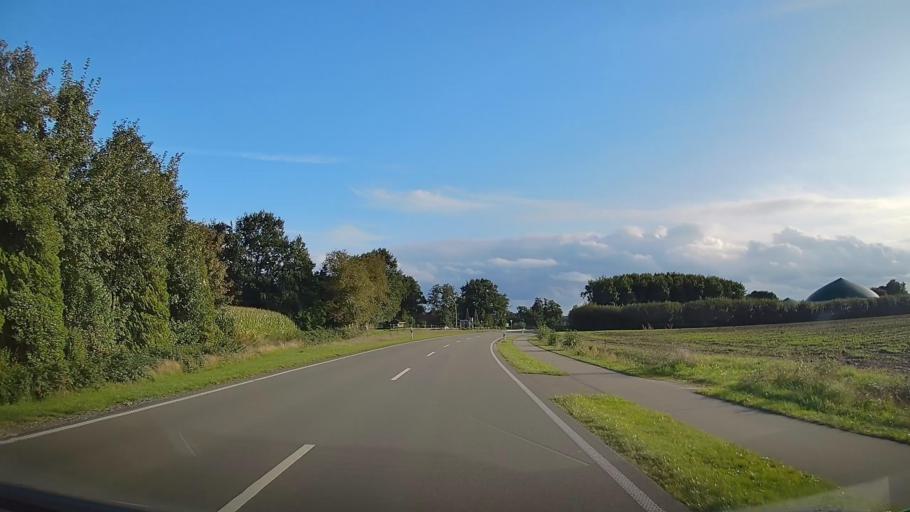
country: DE
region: Lower Saxony
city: Barssel
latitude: 53.0805
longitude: 7.7175
